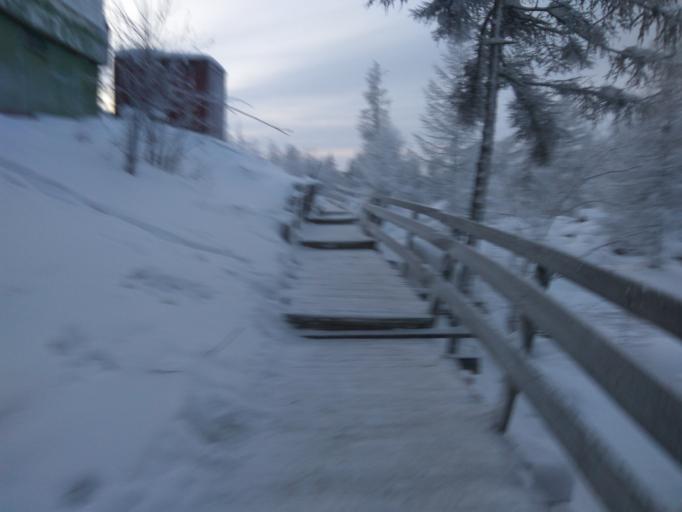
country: RU
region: Sakha
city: Aykhal
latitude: 65.9451
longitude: 111.4969
